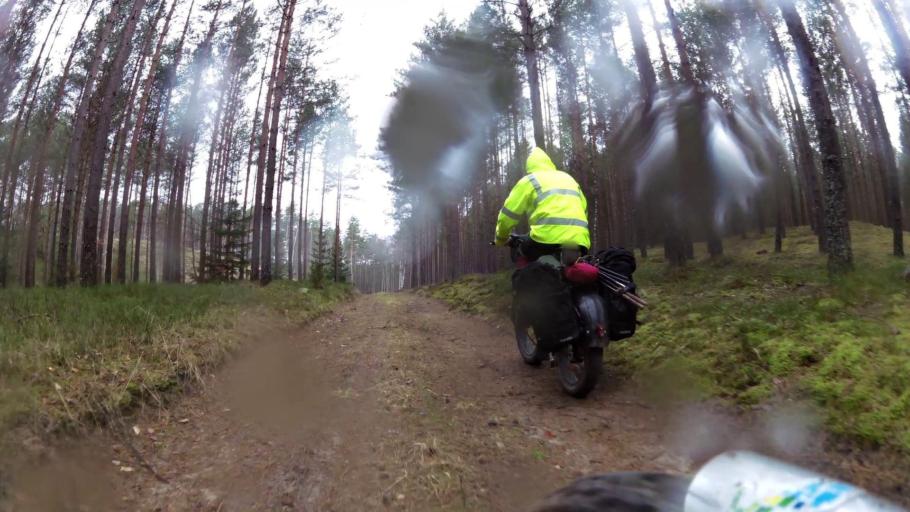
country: PL
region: Pomeranian Voivodeship
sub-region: Powiat bytowski
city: Trzebielino
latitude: 54.0778
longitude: 17.0999
